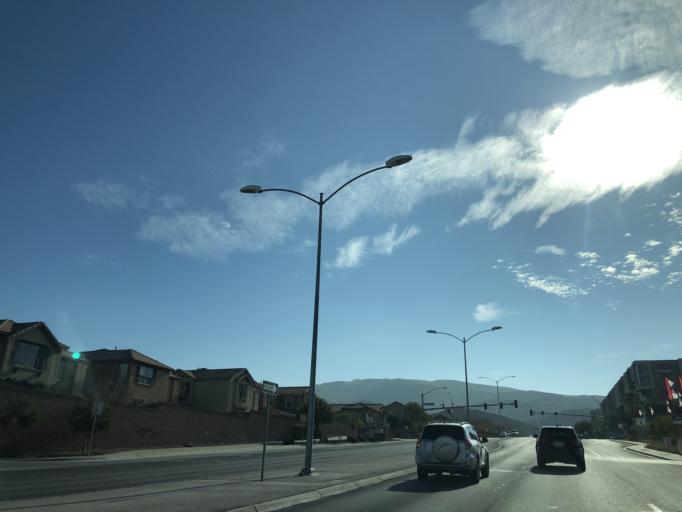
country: US
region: Nevada
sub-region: Clark County
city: Henderson
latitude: 36.0271
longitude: -115.0296
